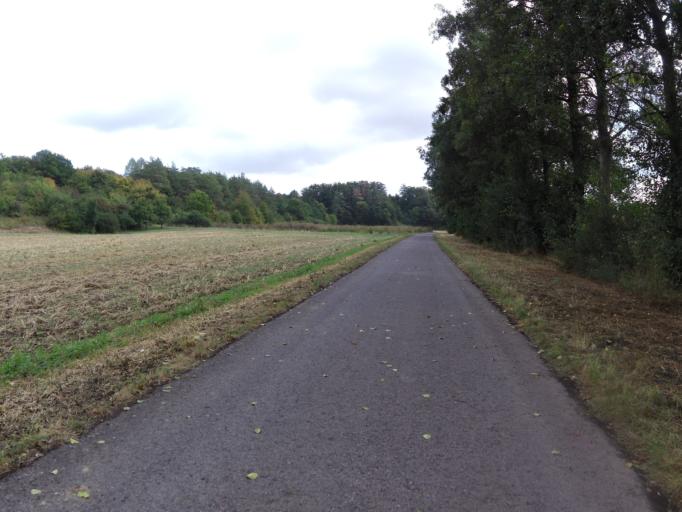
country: DE
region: Bavaria
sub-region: Regierungsbezirk Unterfranken
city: Gadheim
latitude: 49.8554
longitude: 9.9087
